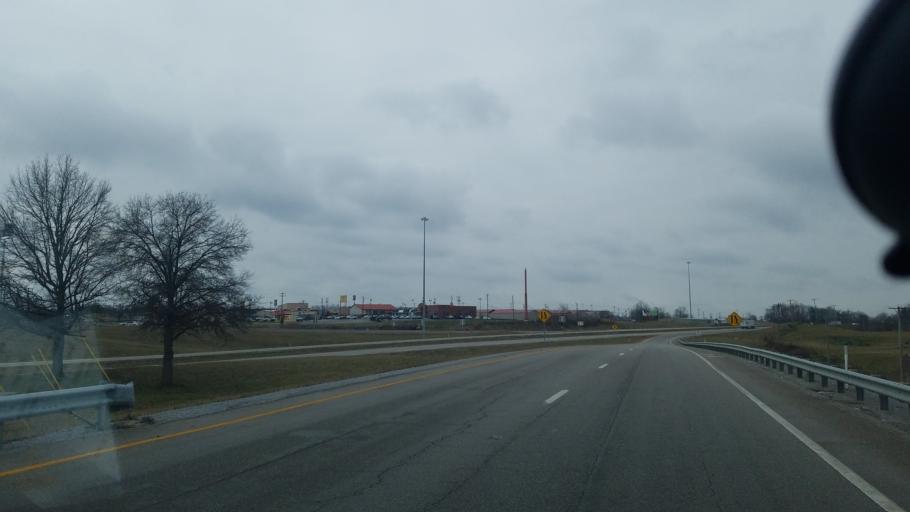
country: US
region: Kentucky
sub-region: Montgomery County
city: Mount Sterling
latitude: 38.0787
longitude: -83.9500
